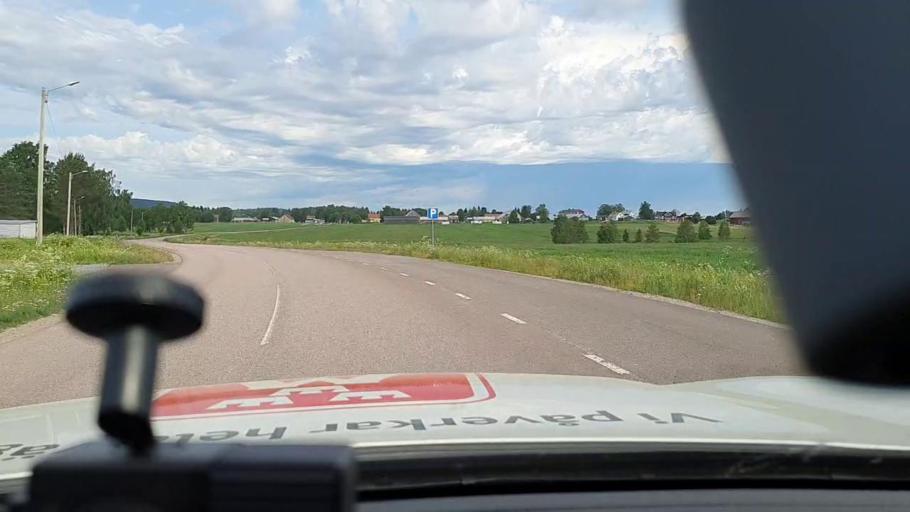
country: SE
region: Norrbotten
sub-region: Bodens Kommun
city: Saevast
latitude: 65.7044
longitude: 21.7678
